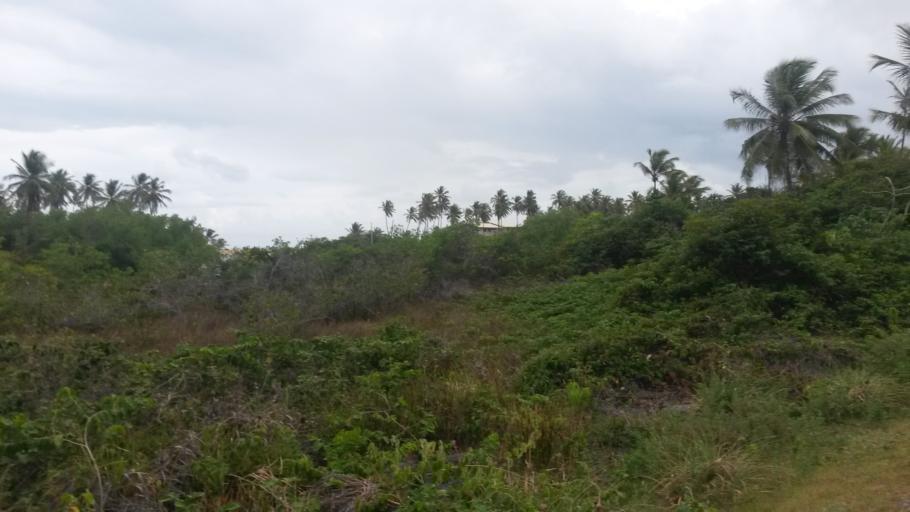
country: BR
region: Bahia
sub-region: Mata De Sao Joao
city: Mata de Sao Joao
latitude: -12.4969
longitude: -37.9610
